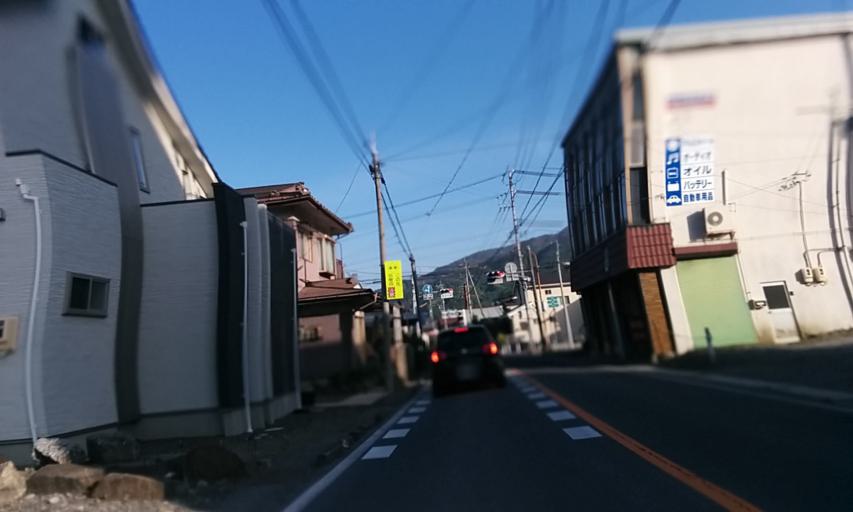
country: JP
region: Nagano
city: Suwa
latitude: 36.0210
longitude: 138.0876
